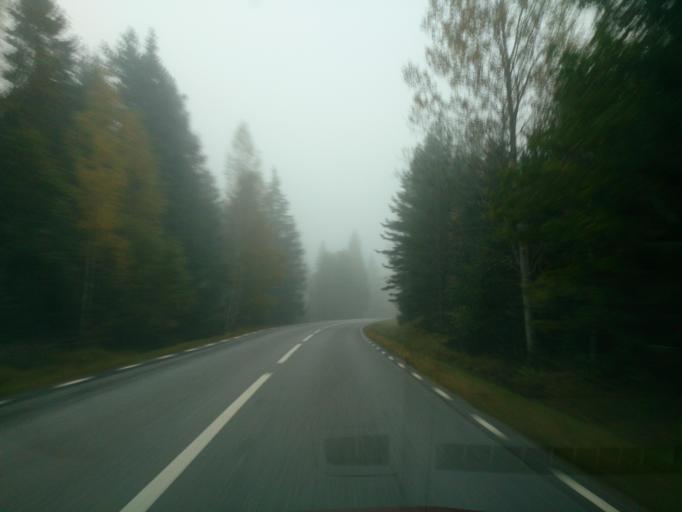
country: SE
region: OEstergoetland
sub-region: Atvidabergs Kommun
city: Atvidaberg
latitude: 58.1470
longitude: 15.9612
